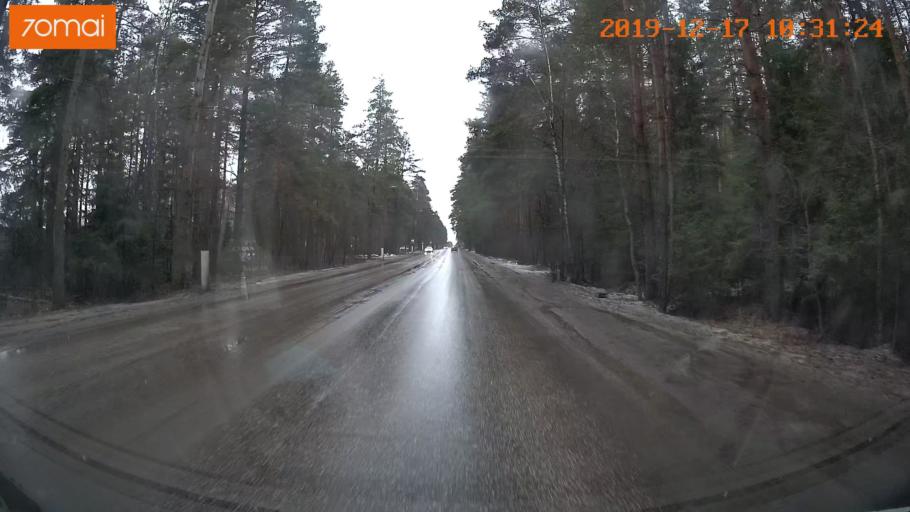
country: RU
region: Vladimir
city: Gus'-Khrustal'nyy
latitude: 55.6357
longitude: 40.6980
